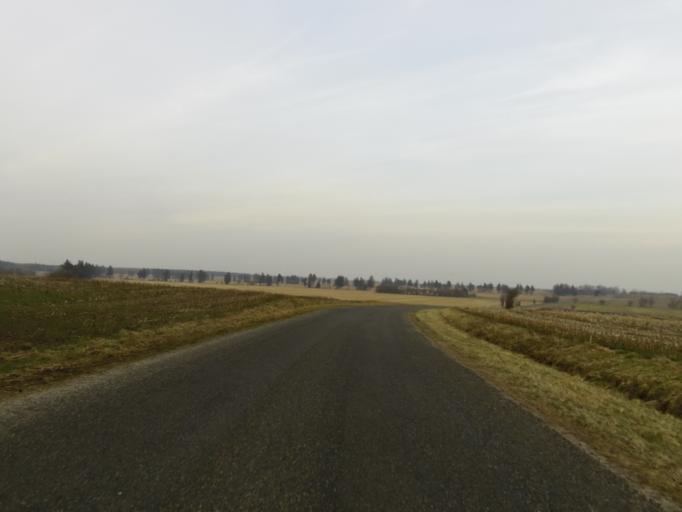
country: DK
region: South Denmark
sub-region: Esbjerg Kommune
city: Ribe
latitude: 55.3462
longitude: 8.9037
